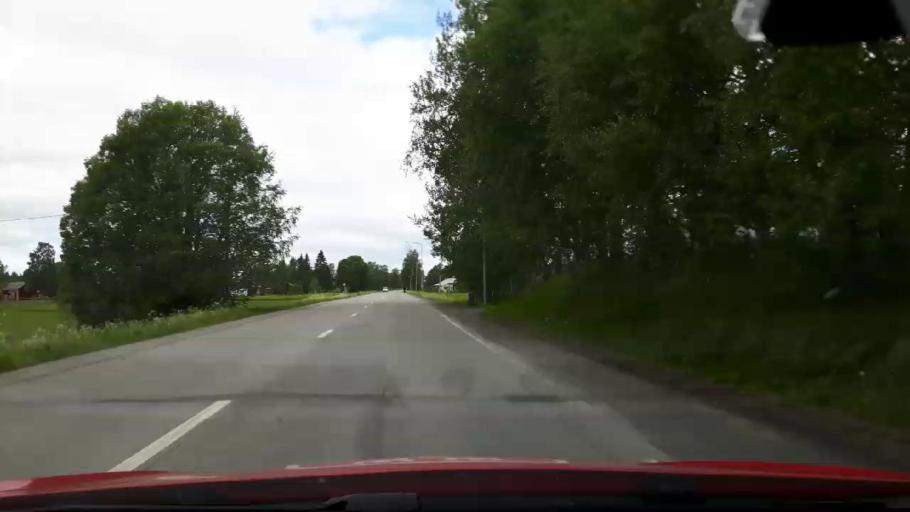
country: SE
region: Jaemtland
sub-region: Krokoms Kommun
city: Krokom
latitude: 63.3079
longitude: 14.4651
